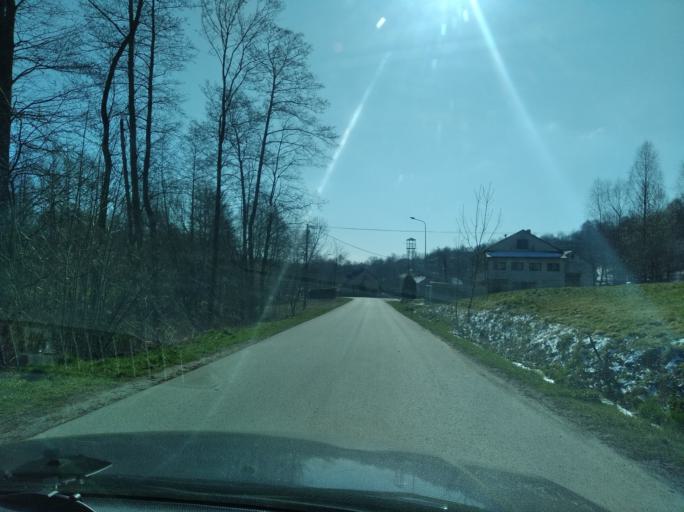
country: PL
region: Subcarpathian Voivodeship
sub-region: Powiat strzyzowski
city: Jawornik
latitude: 49.8490
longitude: 21.8725
